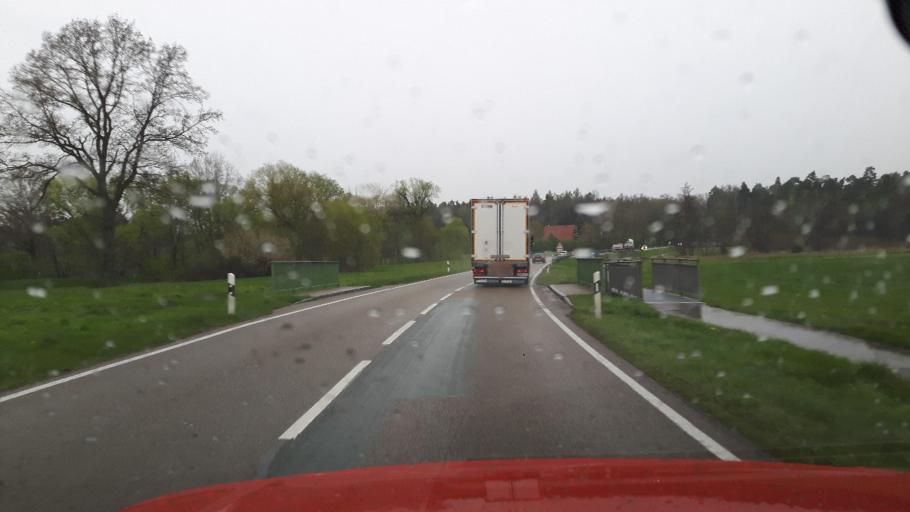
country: DE
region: Bavaria
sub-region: Regierungsbezirk Mittelfranken
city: Muhr am See
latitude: 49.1606
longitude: 10.7159
